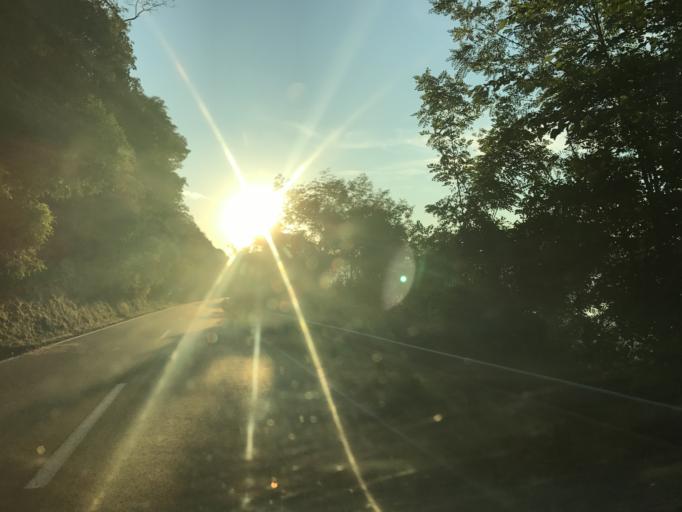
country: RO
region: Caras-Severin
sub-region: Comuna Berzasca
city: Liubcova
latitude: 44.6446
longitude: 21.8767
